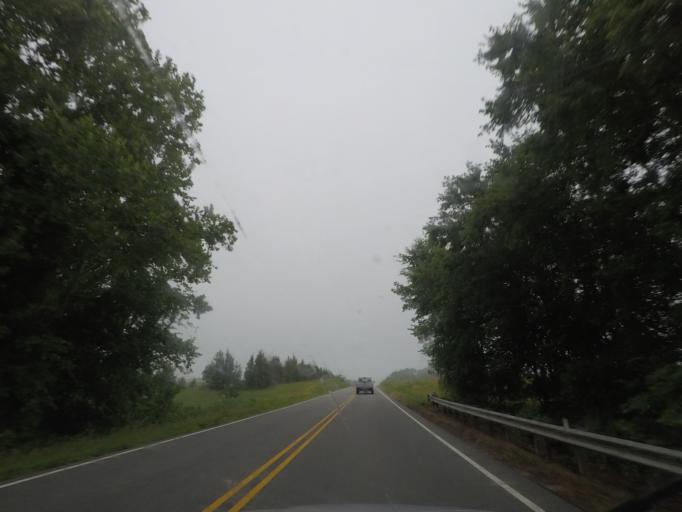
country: US
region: Virginia
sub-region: Prince Edward County
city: Farmville
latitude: 37.3511
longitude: -78.4783
